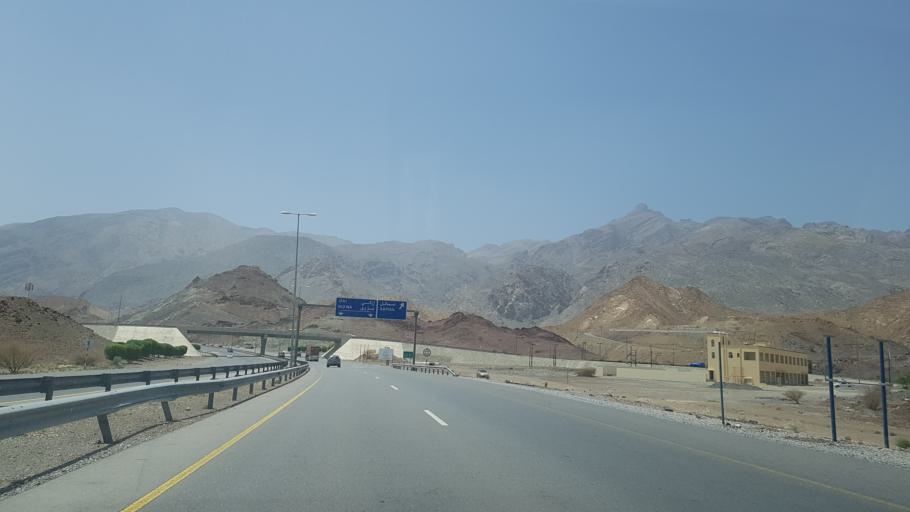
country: OM
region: Muhafazat ad Dakhiliyah
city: Sufalat Sama'il
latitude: 23.3165
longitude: 57.9521
